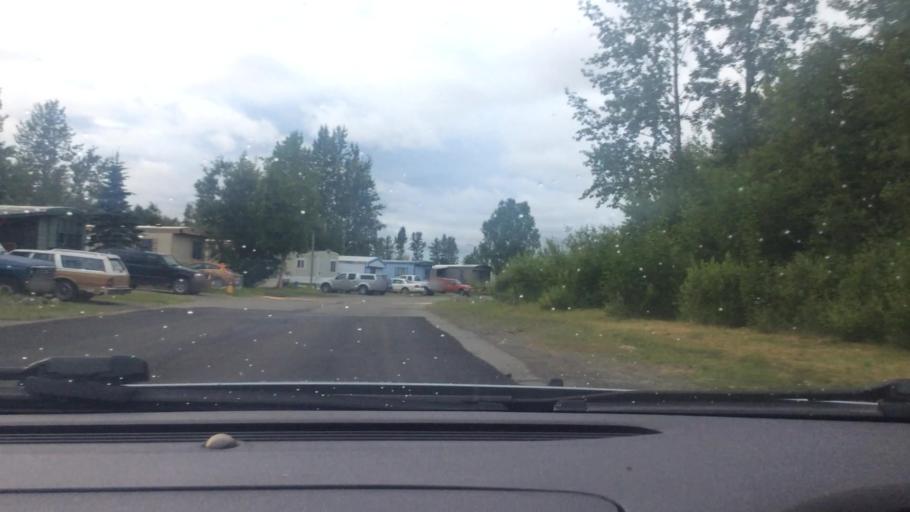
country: US
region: Alaska
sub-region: Anchorage Municipality
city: Elmendorf Air Force Base
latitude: 61.1989
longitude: -149.7255
